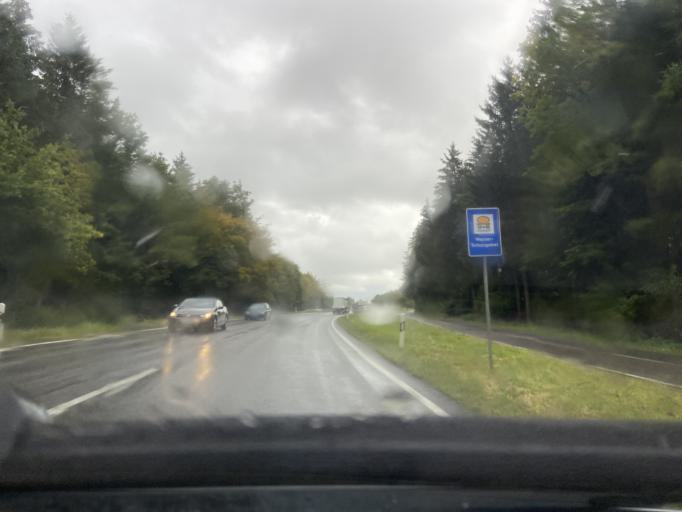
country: DE
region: Baden-Wuerttemberg
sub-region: Freiburg Region
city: Buchheim
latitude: 47.9881
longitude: 9.0202
